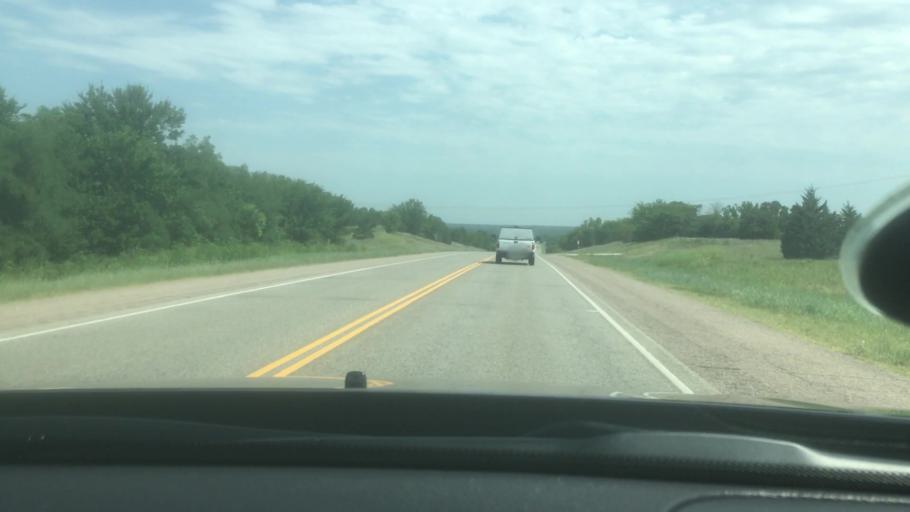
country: US
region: Oklahoma
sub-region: Seminole County
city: Maud
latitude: 35.0575
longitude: -96.9320
